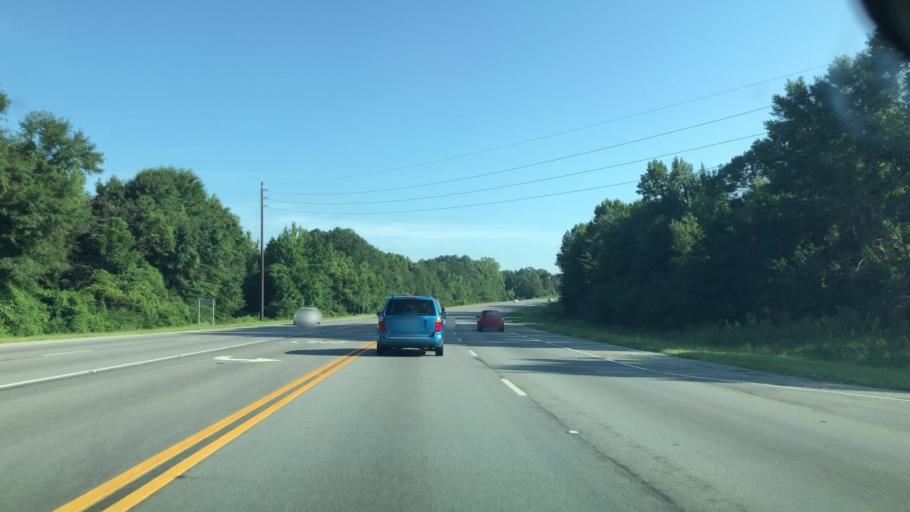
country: US
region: Alabama
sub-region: Calhoun County
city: Bynum
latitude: 33.6074
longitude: -85.9283
